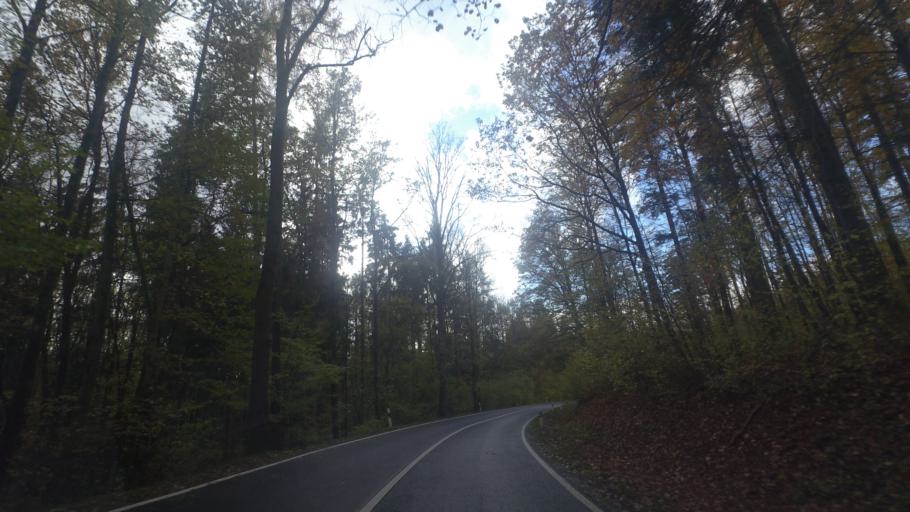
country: DE
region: Thuringia
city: Dingsleben
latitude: 50.4098
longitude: 10.6147
